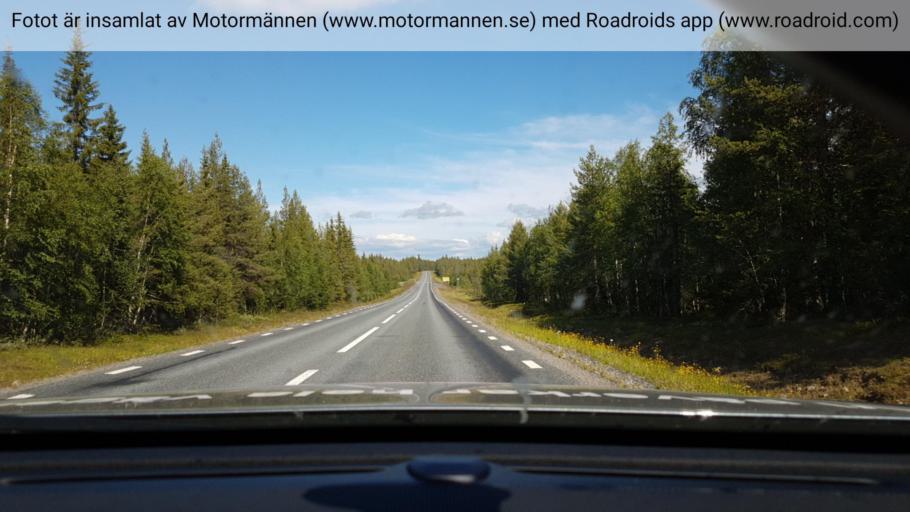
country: SE
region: Vaesterbotten
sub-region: Sorsele Kommun
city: Sorsele
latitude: 65.5647
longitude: 17.9915
